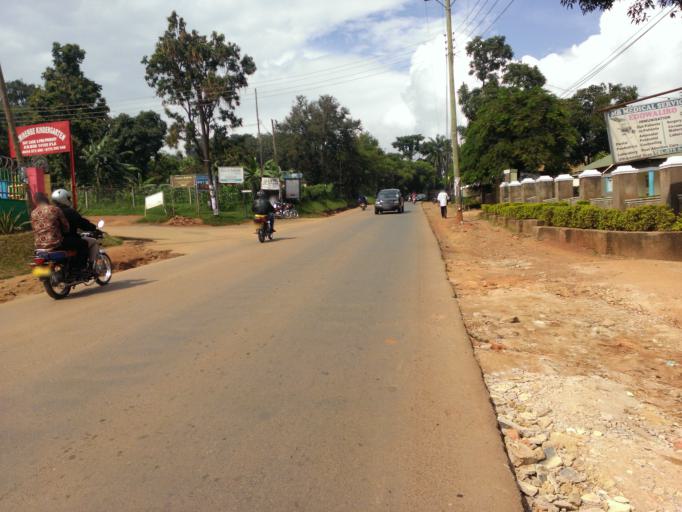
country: UG
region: Central Region
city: Kampala Central Division
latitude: 0.3230
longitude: 32.5599
